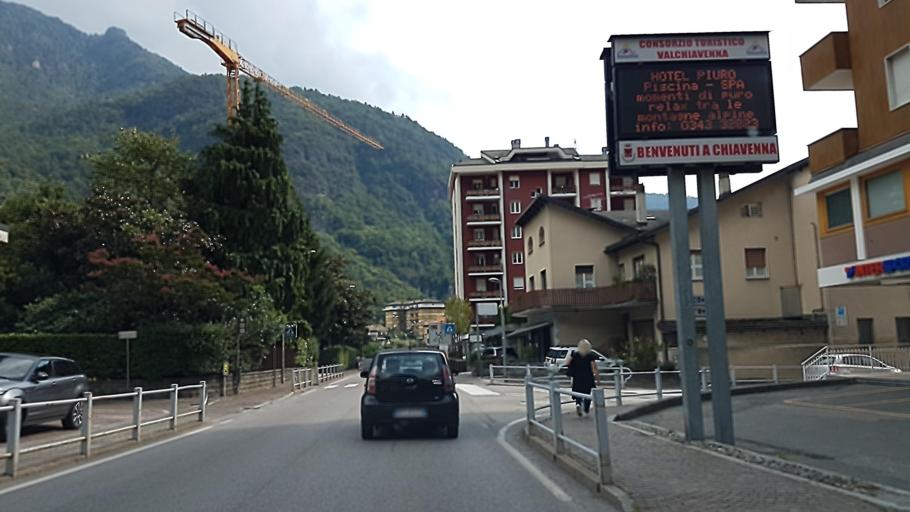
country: IT
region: Lombardy
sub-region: Provincia di Sondrio
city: Chiavenna
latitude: 46.3200
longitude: 9.3985
